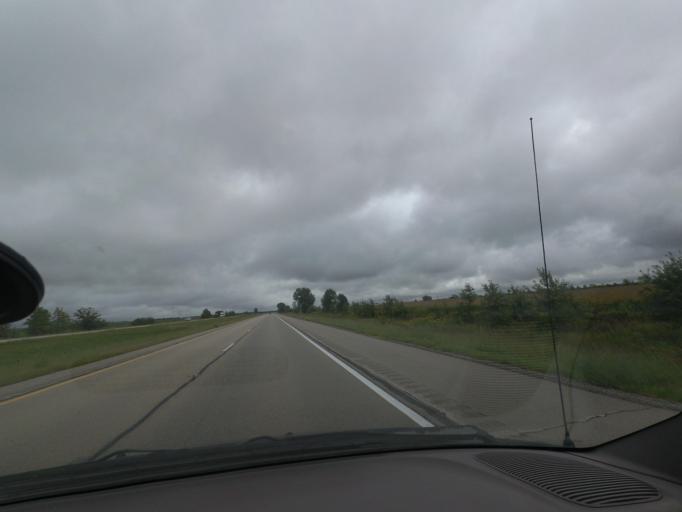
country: US
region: Illinois
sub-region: Piatt County
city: Monticello
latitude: 40.0286
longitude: -88.6561
